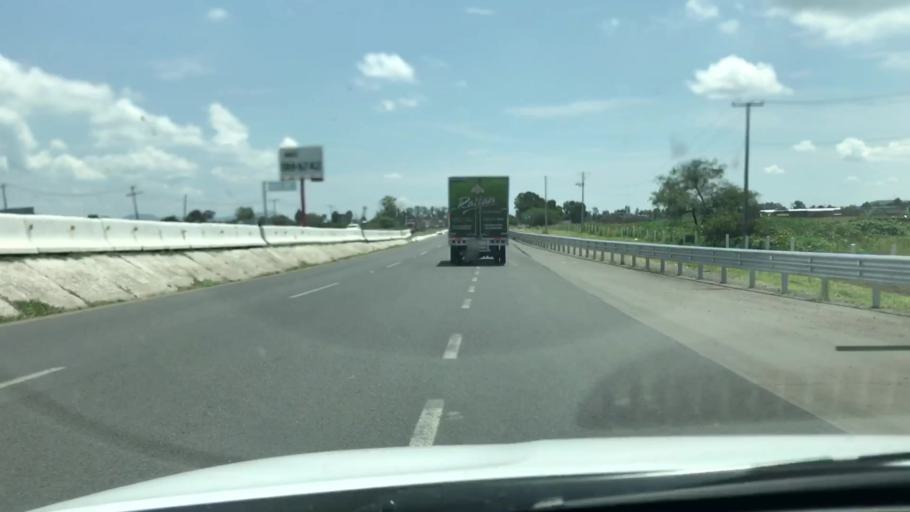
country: MX
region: Guanajuato
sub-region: Irapuato
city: Las Huertas Tercera Seccion
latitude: 20.6496
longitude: -101.3716
